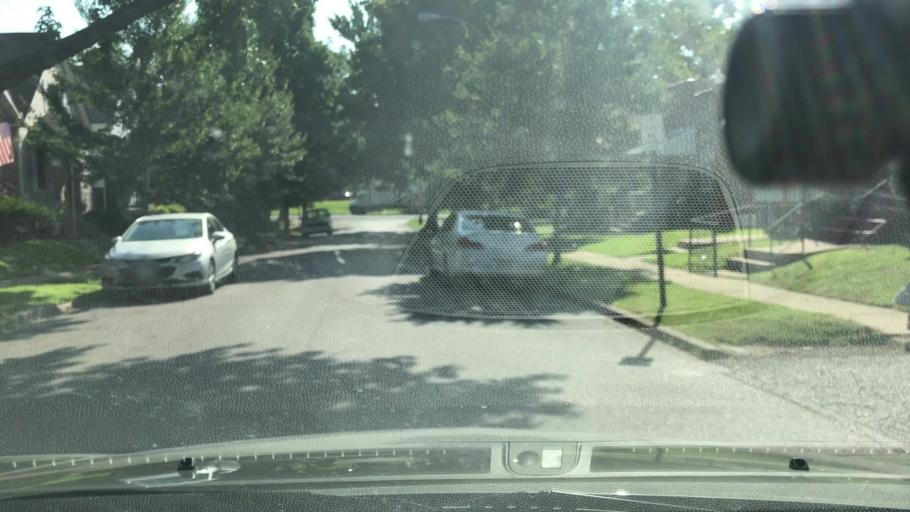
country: US
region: Missouri
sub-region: Saint Louis County
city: Lemay
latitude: 38.5785
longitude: -90.2768
